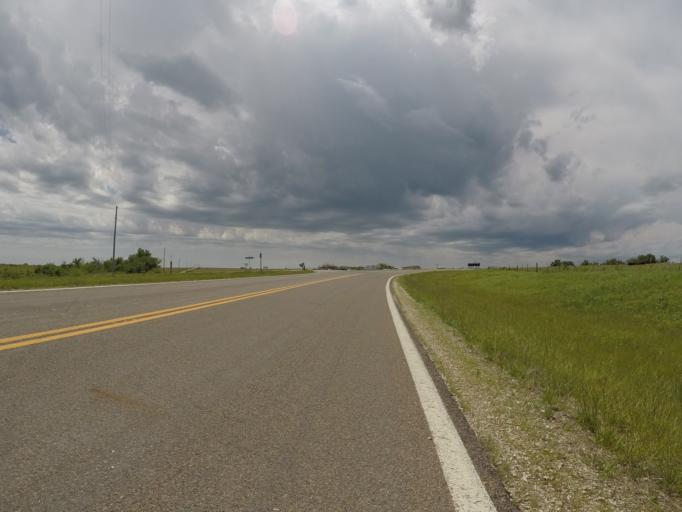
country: US
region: Kansas
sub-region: Wabaunsee County
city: Alma
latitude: 38.8575
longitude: -96.3730
